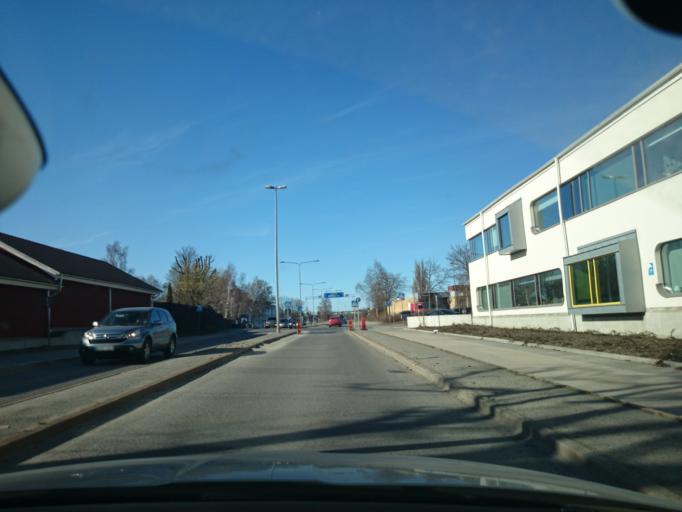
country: SE
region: Stockholm
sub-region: Huddinge Kommun
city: Segeltorp
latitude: 59.2782
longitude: 17.9439
